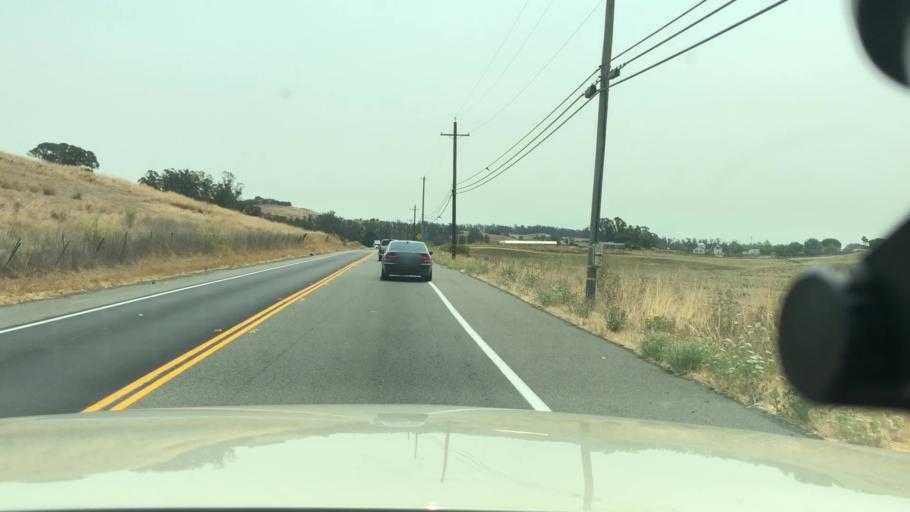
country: US
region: California
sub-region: Sonoma County
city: Petaluma
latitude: 38.2175
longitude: -122.5585
